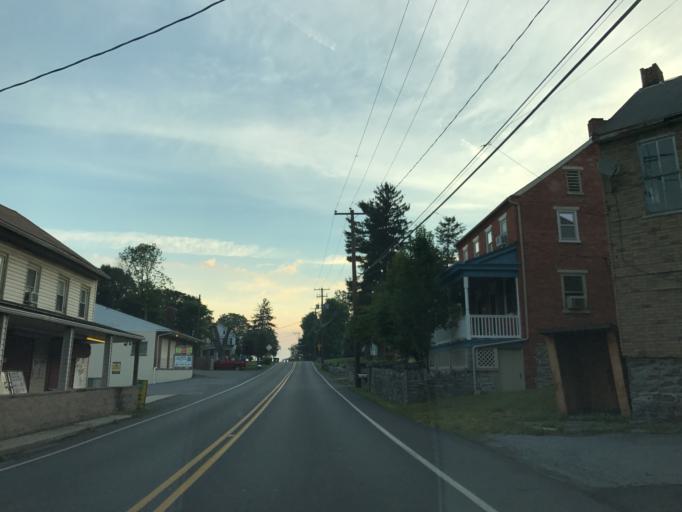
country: US
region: Pennsylvania
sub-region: Lancaster County
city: Willow Street
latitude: 39.9866
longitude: -76.3149
